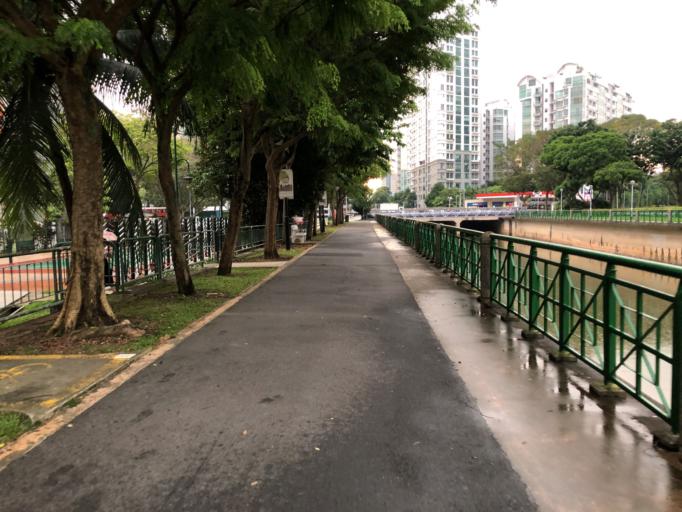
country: SG
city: Singapore
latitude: 1.2923
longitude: 103.8270
